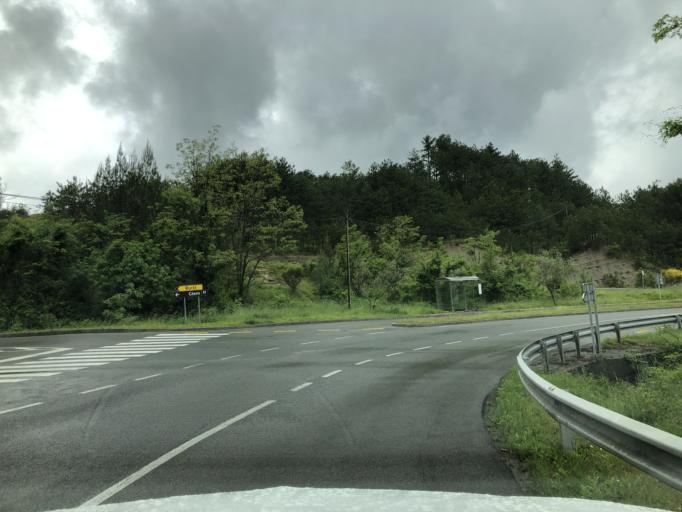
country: SI
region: Koper-Capodistria
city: Prade
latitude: 45.5007
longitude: 13.7829
